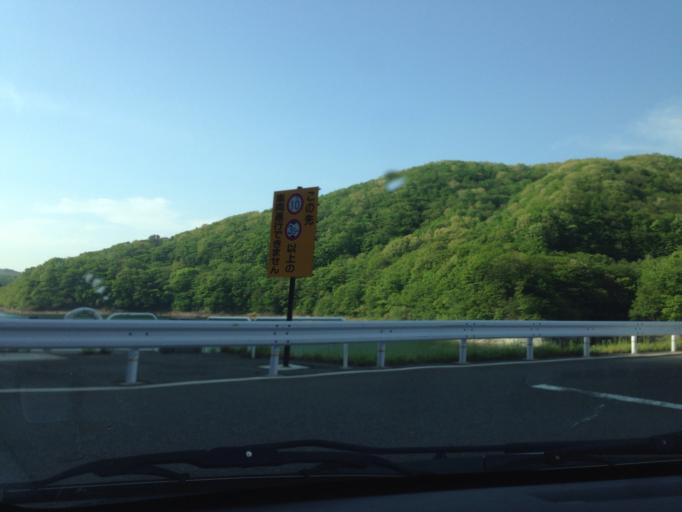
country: JP
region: Fukushima
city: Inawashiro
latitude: 37.2724
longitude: 140.0767
